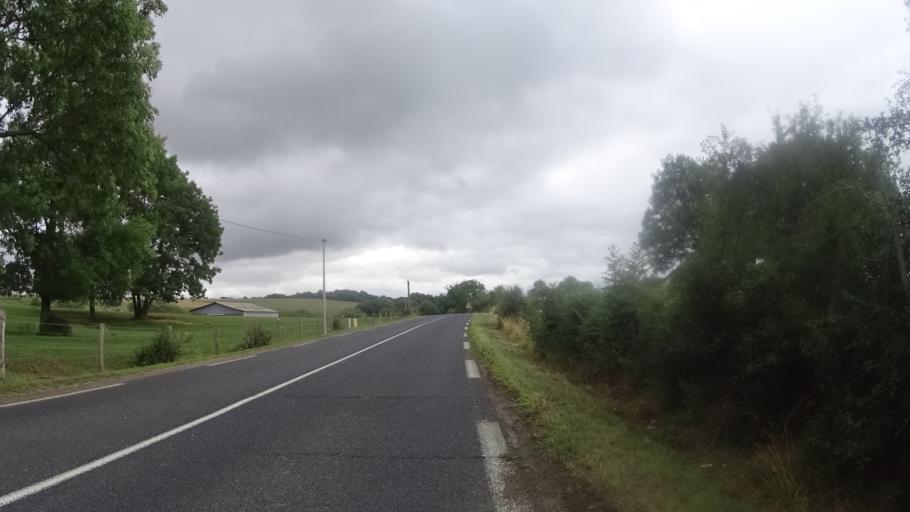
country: FR
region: Lorraine
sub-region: Departement de Meurthe-et-Moselle
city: Art-sur-Meurthe
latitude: 48.6495
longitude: 6.2738
